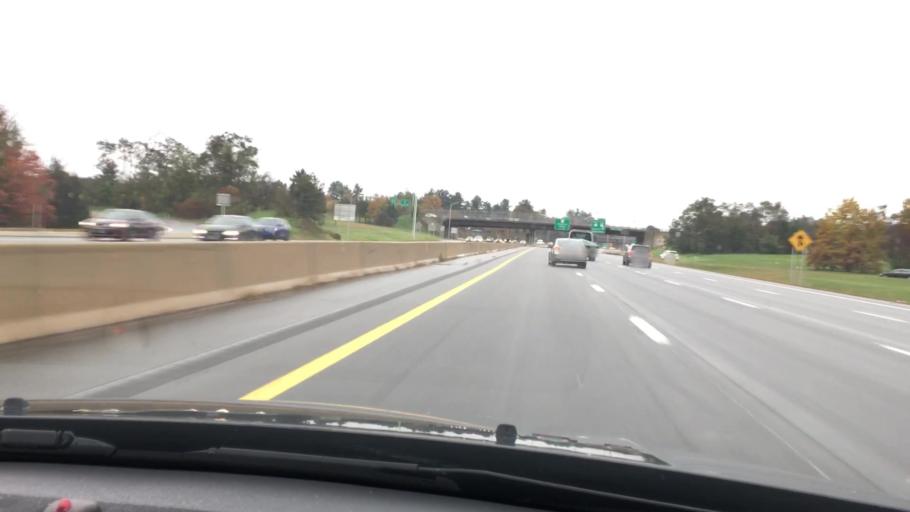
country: US
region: New Hampshire
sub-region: Hillsborough County
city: Nashua
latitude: 42.7794
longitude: -71.4936
